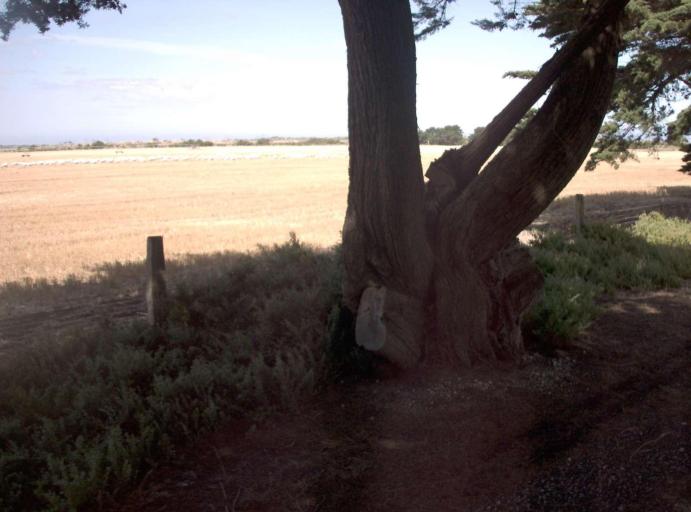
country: AU
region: Victoria
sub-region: Wellington
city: Sale
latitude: -38.3649
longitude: 147.1854
